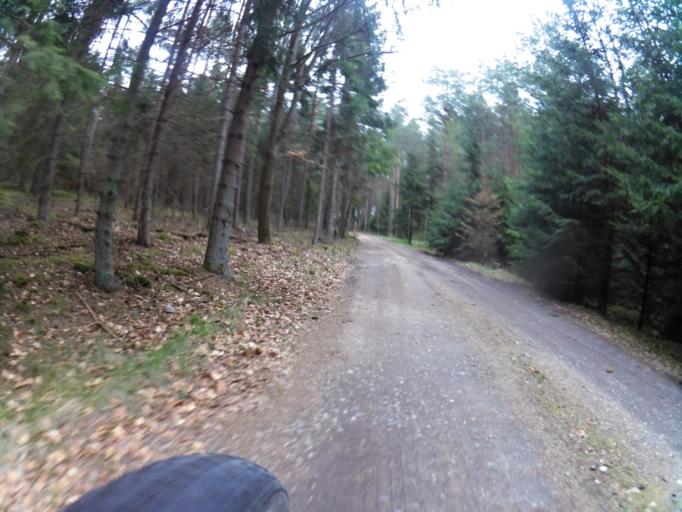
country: PL
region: West Pomeranian Voivodeship
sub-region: Powiat koszalinski
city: Polanow
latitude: 54.1826
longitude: 16.6746
